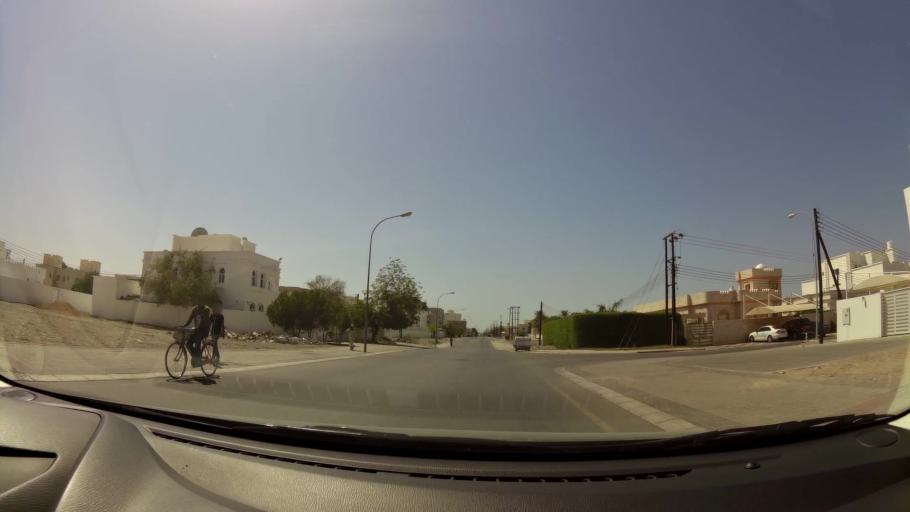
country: OM
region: Muhafazat Masqat
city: As Sib al Jadidah
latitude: 23.6300
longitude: 58.2184
